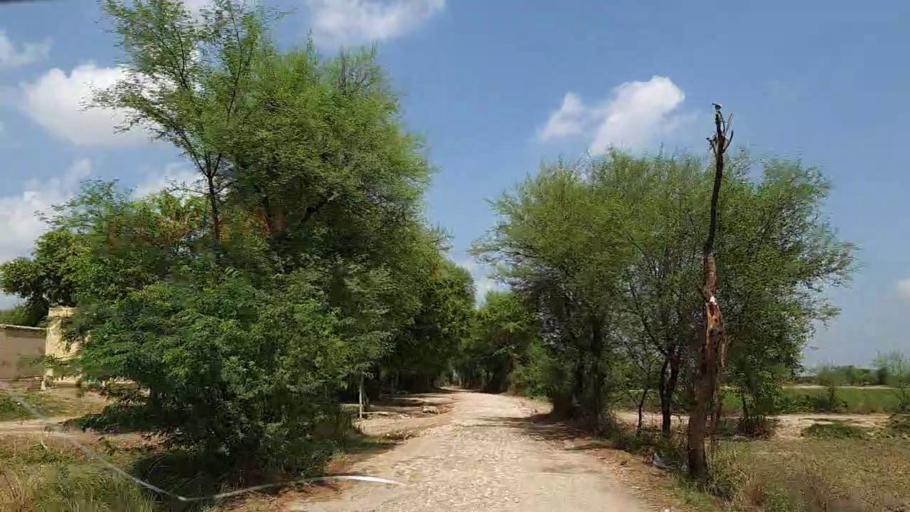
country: PK
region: Sindh
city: Tharu Shah
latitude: 26.9990
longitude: 68.0648
